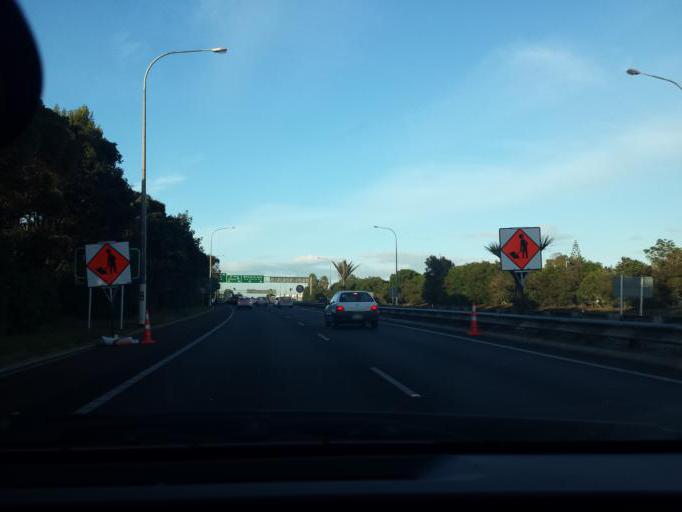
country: NZ
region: Auckland
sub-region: Auckland
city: Mangere
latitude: -36.9712
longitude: 174.7910
